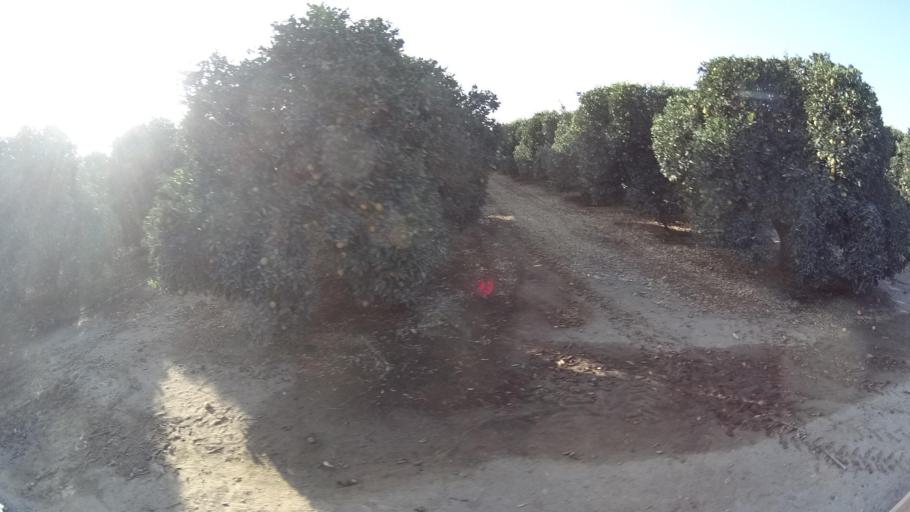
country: US
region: California
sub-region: Tulare County
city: Richgrove
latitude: 35.7763
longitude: -119.0824
